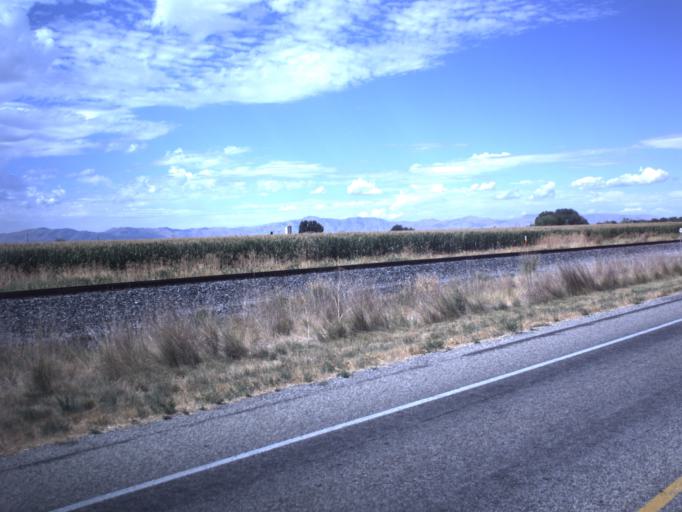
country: US
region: Utah
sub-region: Box Elder County
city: Brigham City
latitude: 41.5405
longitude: -112.0842
